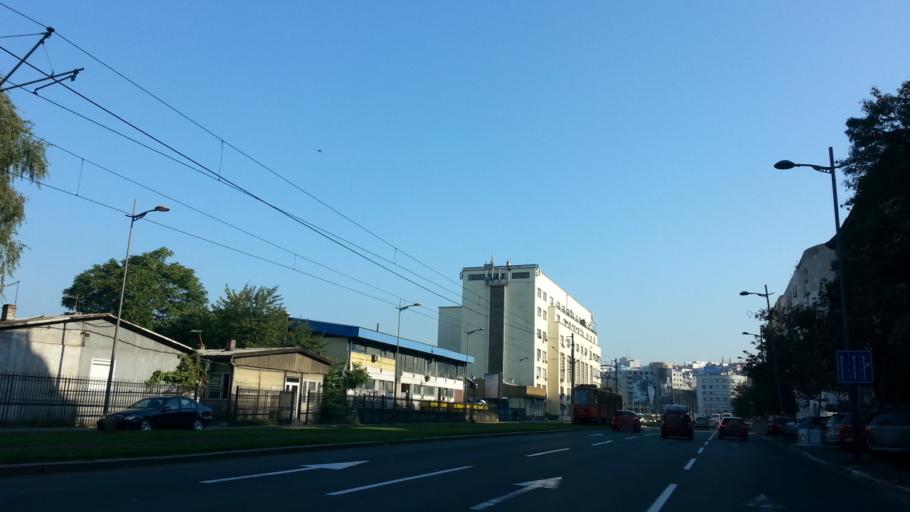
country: RS
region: Central Serbia
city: Belgrade
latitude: 44.8058
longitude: 20.4544
